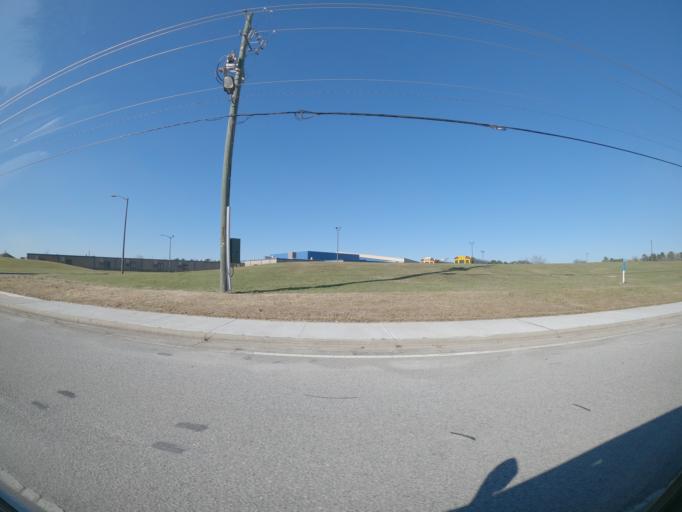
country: US
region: Georgia
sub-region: Columbia County
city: Grovetown
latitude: 33.4521
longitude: -82.2205
